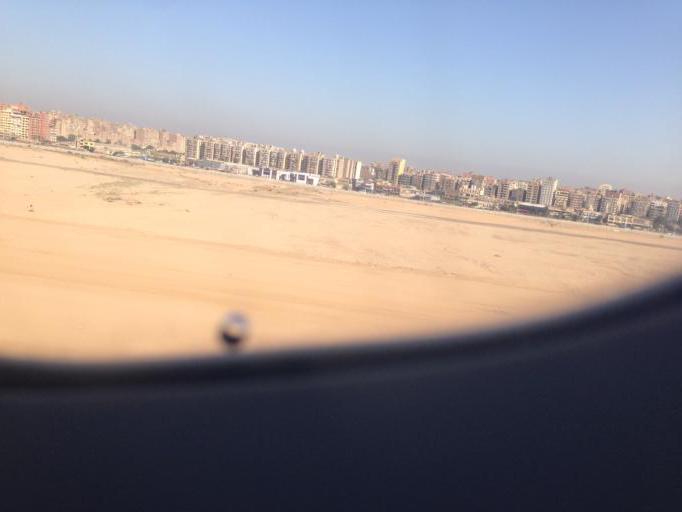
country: EG
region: Muhafazat al Qalyubiyah
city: Al Khankah
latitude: 30.1337
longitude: 31.3992
